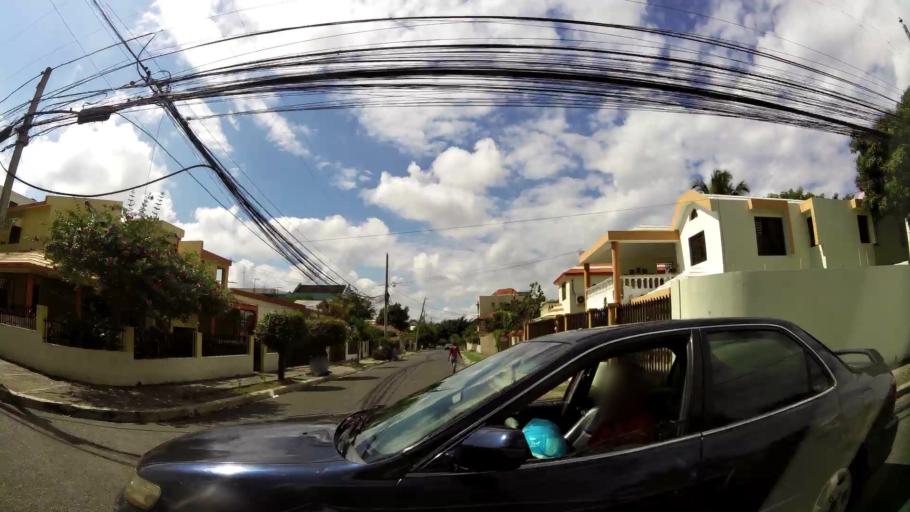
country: DO
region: Santiago
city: Santiago de los Caballeros
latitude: 19.4706
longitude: -70.6924
